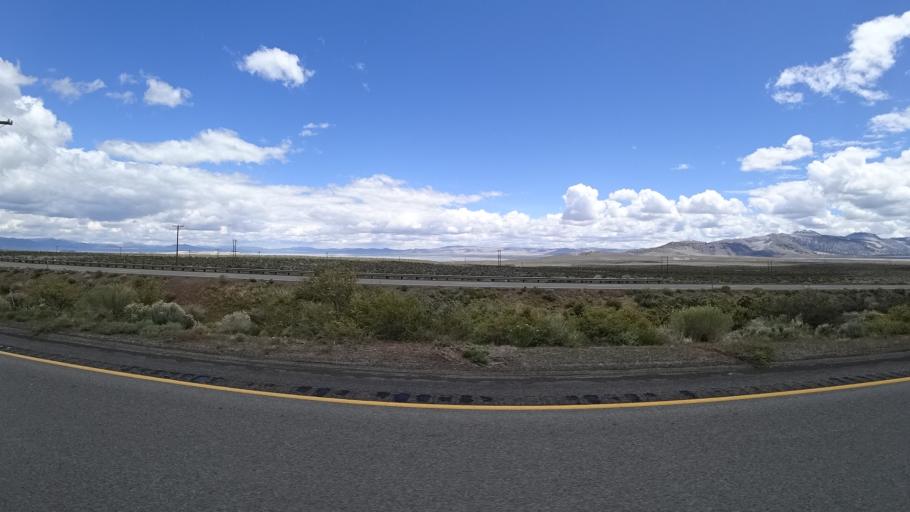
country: US
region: California
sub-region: Mono County
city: Mammoth Lakes
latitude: 37.9390
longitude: -119.1021
